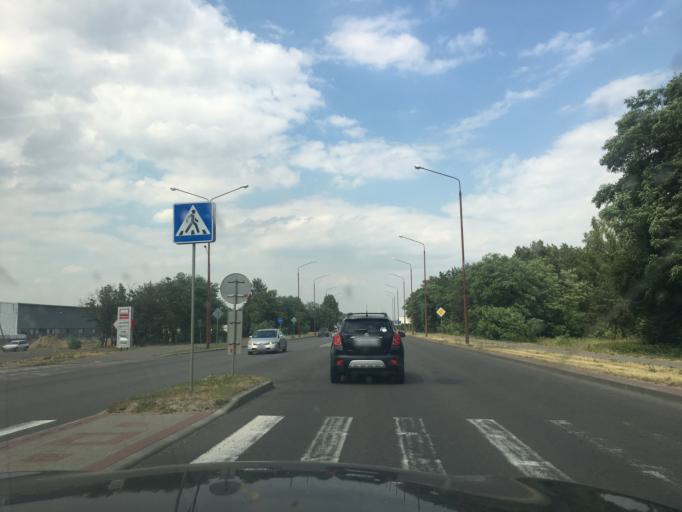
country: BY
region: Brest
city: Brest
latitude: 52.1440
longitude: 23.6829
